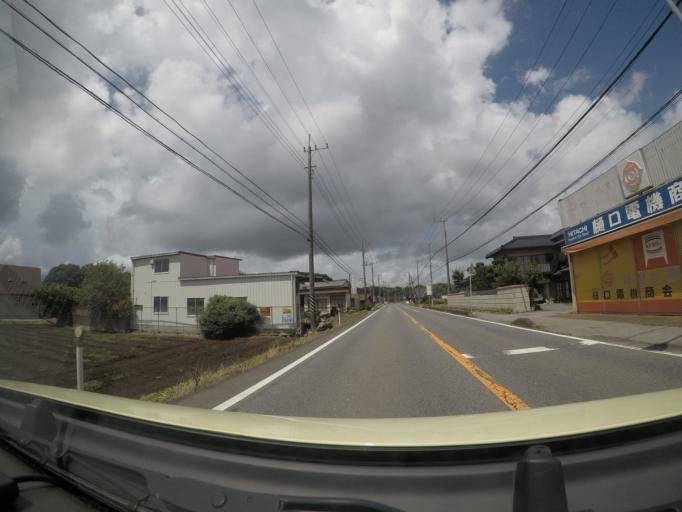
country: JP
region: Ibaraki
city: Mitsukaido
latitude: 36.0327
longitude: 139.9429
